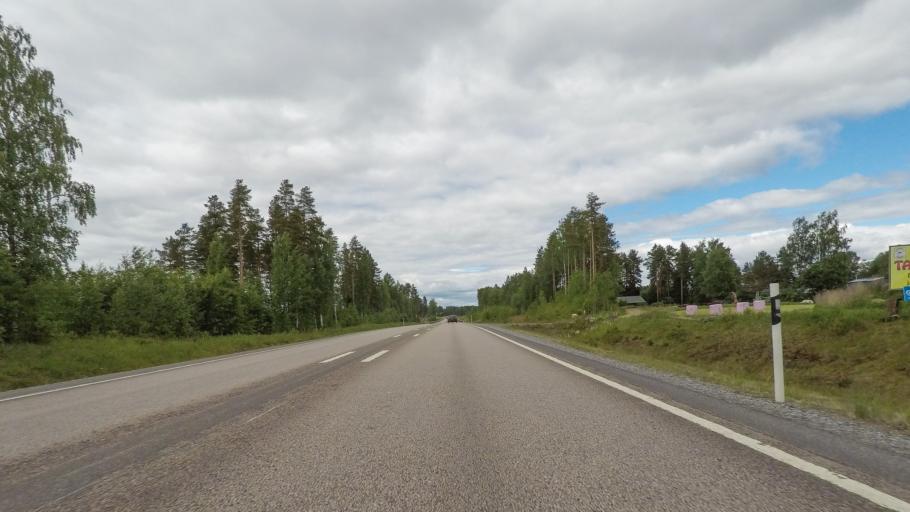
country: FI
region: Paijanne Tavastia
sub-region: Lahti
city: Hartola
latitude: 61.4924
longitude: 25.9794
